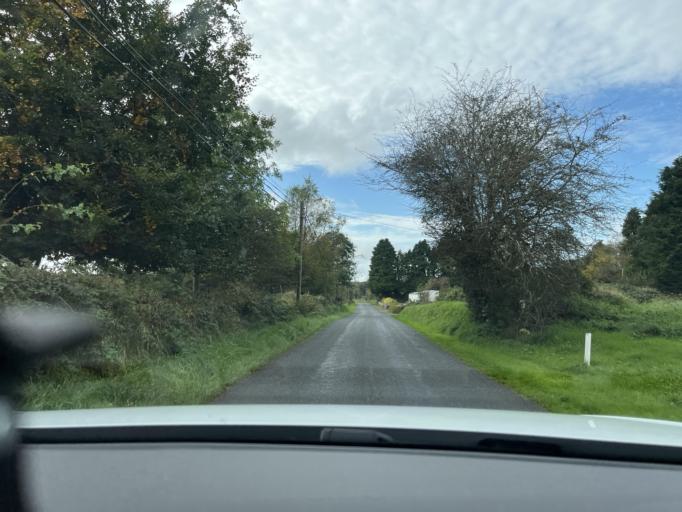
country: IE
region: Connaught
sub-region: Roscommon
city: Boyle
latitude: 54.0240
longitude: -8.3959
